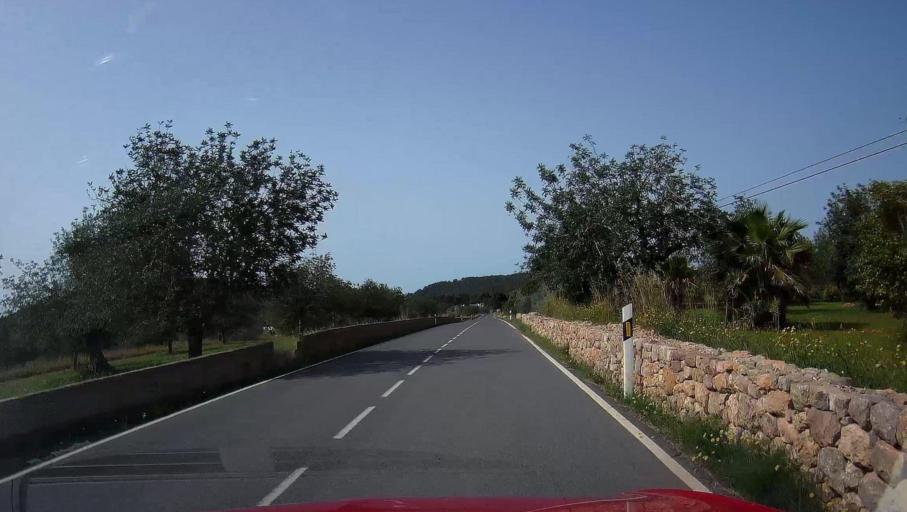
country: ES
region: Balearic Islands
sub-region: Illes Balears
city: Sant Joan de Labritja
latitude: 39.0523
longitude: 1.5742
